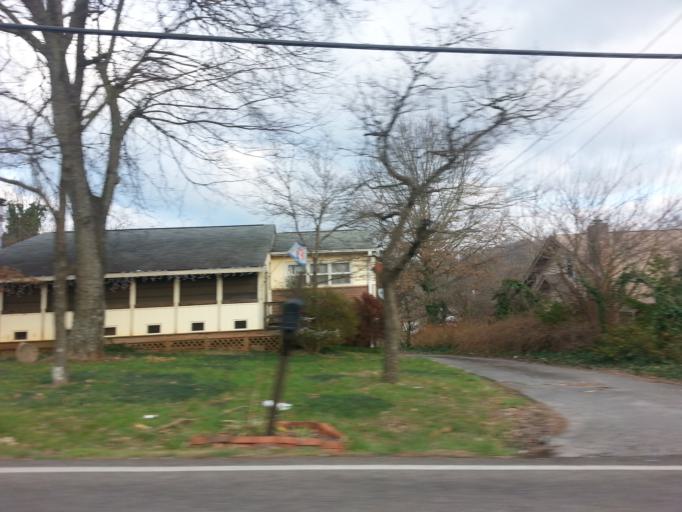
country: US
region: Tennessee
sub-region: Knox County
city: Knoxville
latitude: 35.9467
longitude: -83.8909
